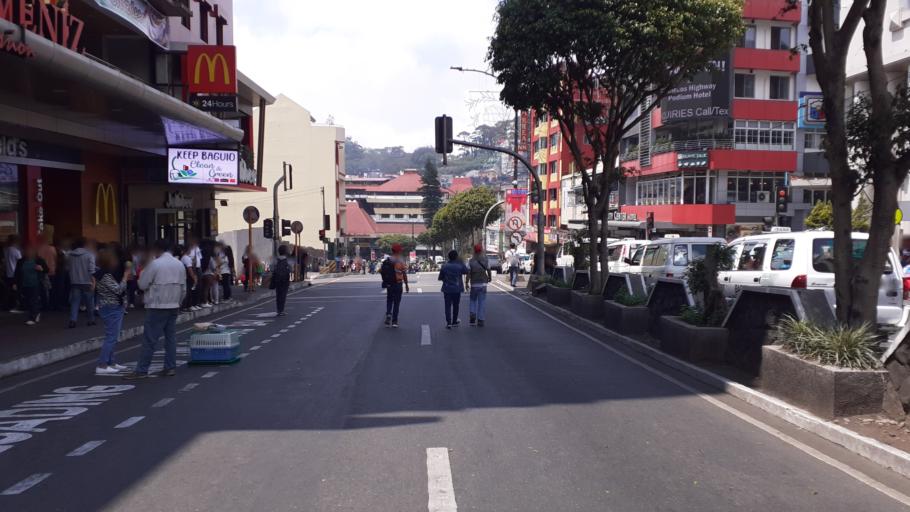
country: PH
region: Cordillera
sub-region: Baguio City
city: Baguio
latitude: 16.4130
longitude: 120.5968
